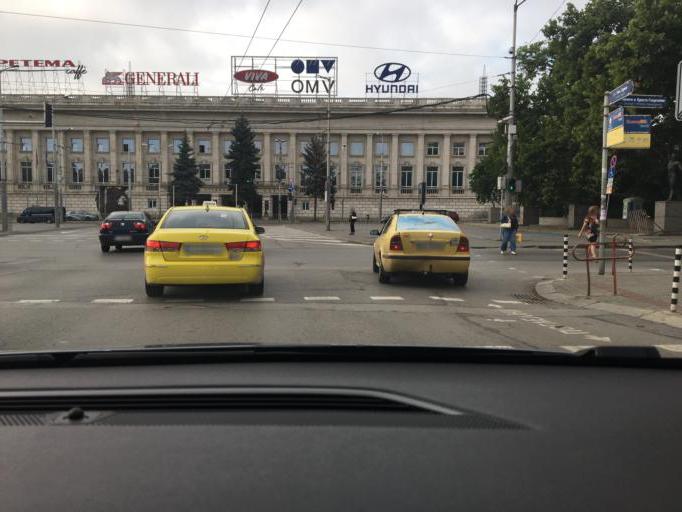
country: BG
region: Sofia-Capital
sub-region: Stolichna Obshtina
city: Sofia
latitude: 42.6886
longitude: 23.3337
